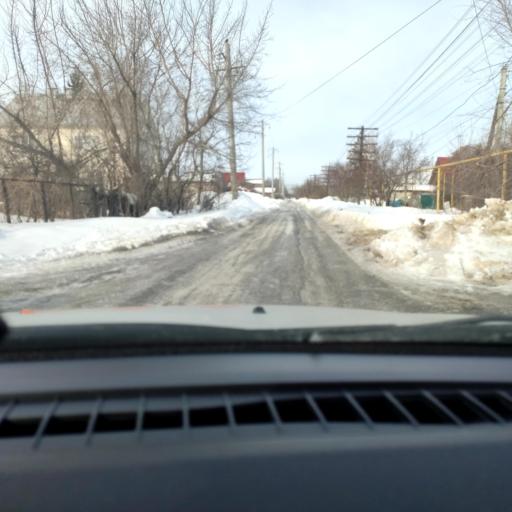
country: RU
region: Samara
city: Kinel'
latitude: 53.2329
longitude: 50.6310
